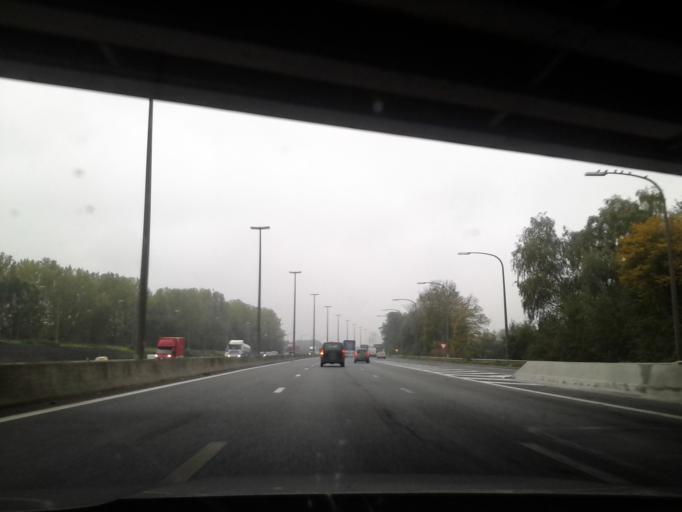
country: BE
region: Wallonia
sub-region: Province du Hainaut
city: Quaregnon
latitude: 50.4540
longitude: 3.9058
